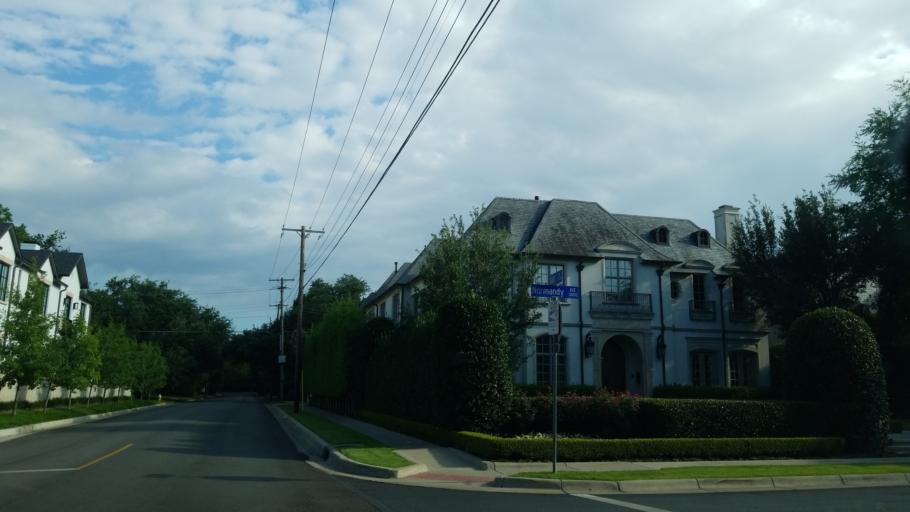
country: US
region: Texas
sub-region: Dallas County
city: Highland Park
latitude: 32.8389
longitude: -96.7956
